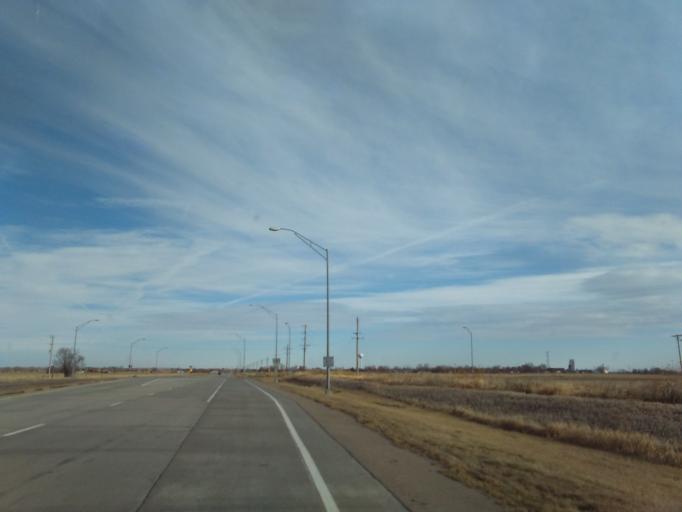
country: US
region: Nebraska
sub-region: Scotts Bluff County
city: Gering
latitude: 41.8147
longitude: -103.5218
